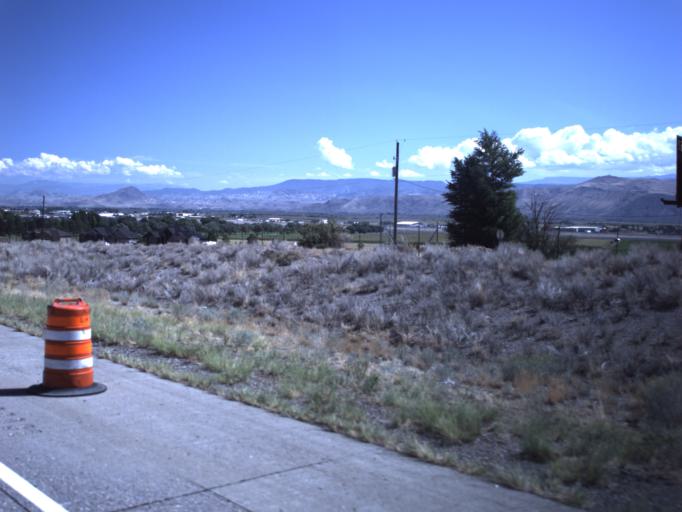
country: US
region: Utah
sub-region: Sevier County
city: Richfield
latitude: 38.7350
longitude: -112.1165
